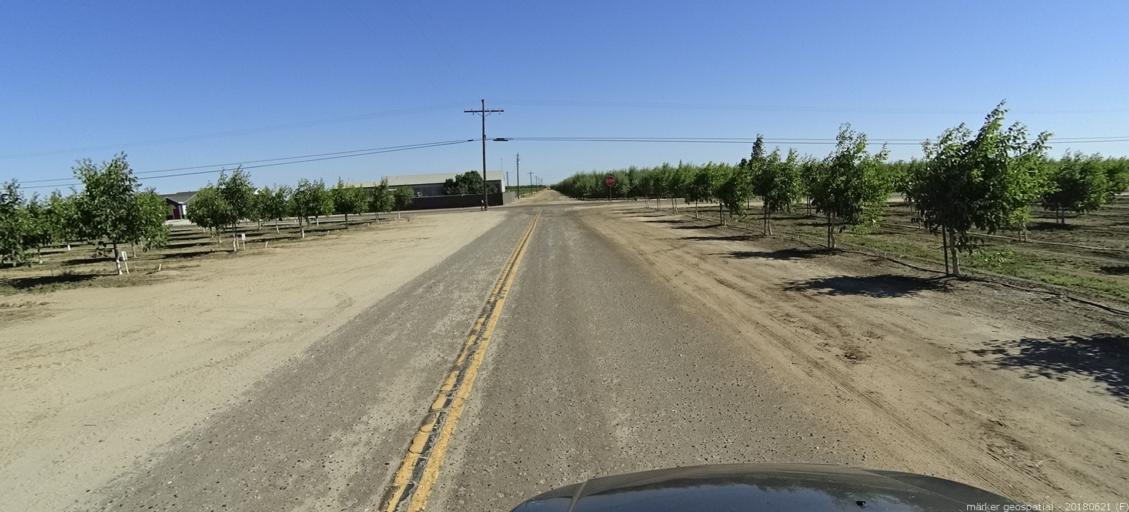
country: US
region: California
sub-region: Fresno County
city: Biola
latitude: 36.8507
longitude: -120.0464
